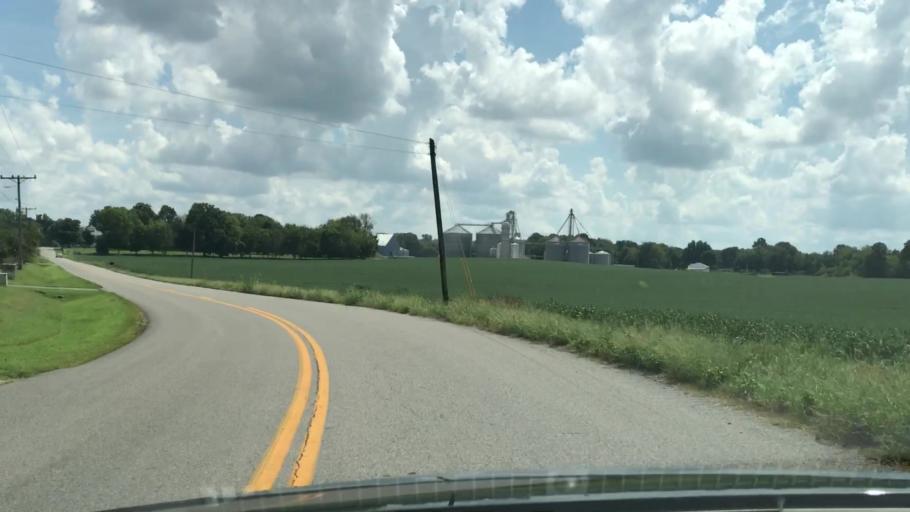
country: US
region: Kentucky
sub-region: Todd County
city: Guthrie
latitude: 36.7186
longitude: -87.0765
